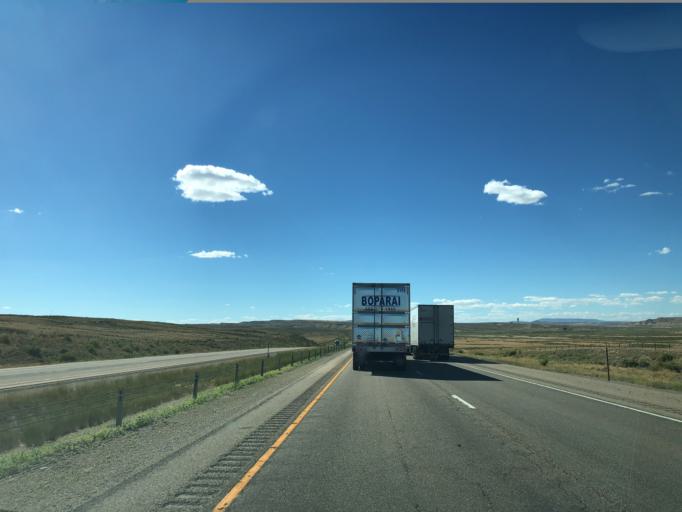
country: US
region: Wyoming
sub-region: Sweetwater County
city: Rock Springs
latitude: 41.6565
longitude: -108.7126
